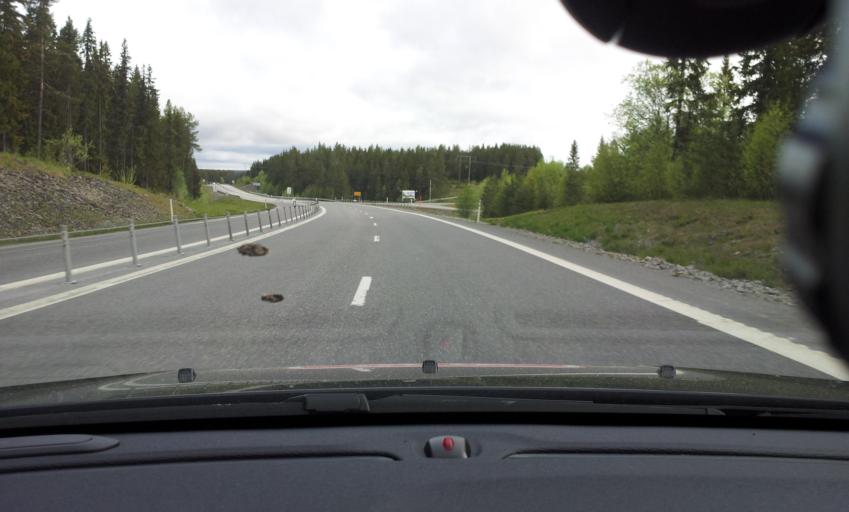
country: SE
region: Jaemtland
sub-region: OEstersunds Kommun
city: Brunflo
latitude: 63.1167
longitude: 14.7982
